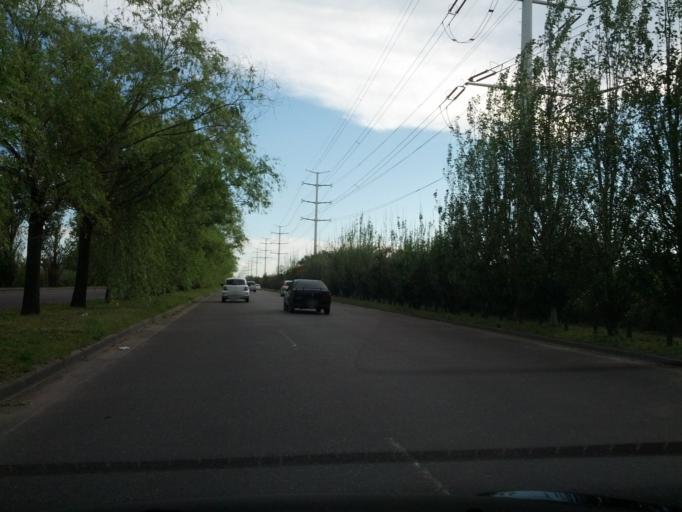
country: AR
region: Buenos Aires F.D.
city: Villa Lugano
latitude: -34.6868
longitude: -58.4461
